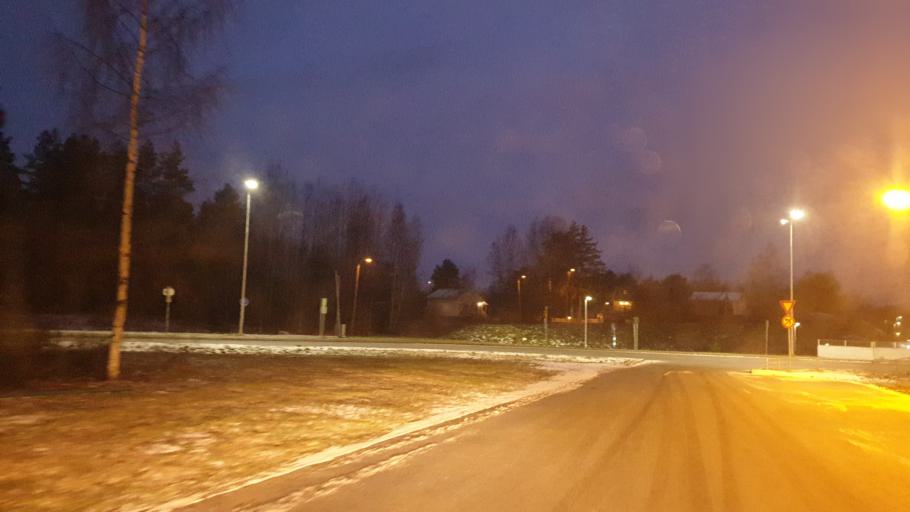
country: FI
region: Southern Savonia
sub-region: Savonlinna
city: Savonlinna
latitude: 61.8773
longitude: 28.8245
